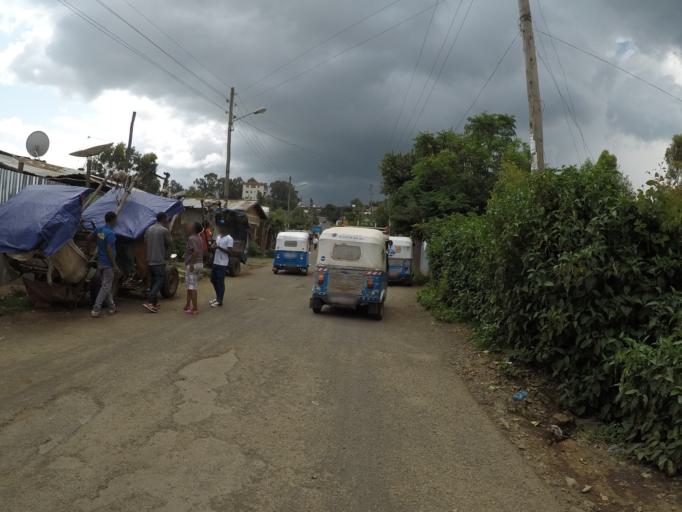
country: ET
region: Amhara
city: Gondar
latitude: 12.6144
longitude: 37.4768
